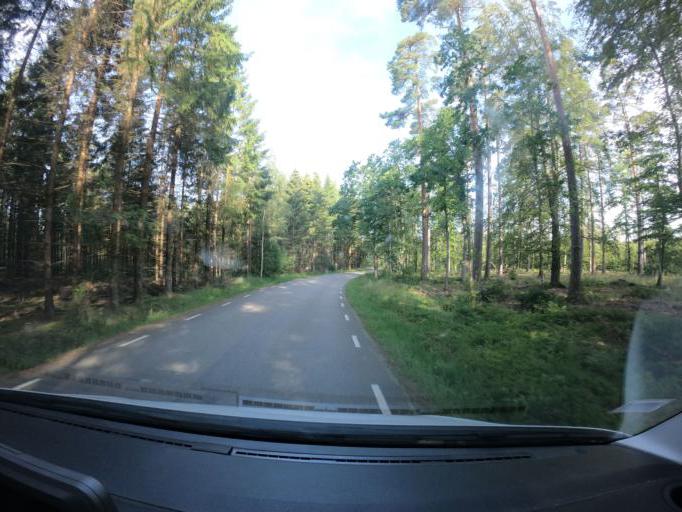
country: SE
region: Skane
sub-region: Angelholms Kommun
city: Munka-Ljungby
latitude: 56.3107
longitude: 13.0373
